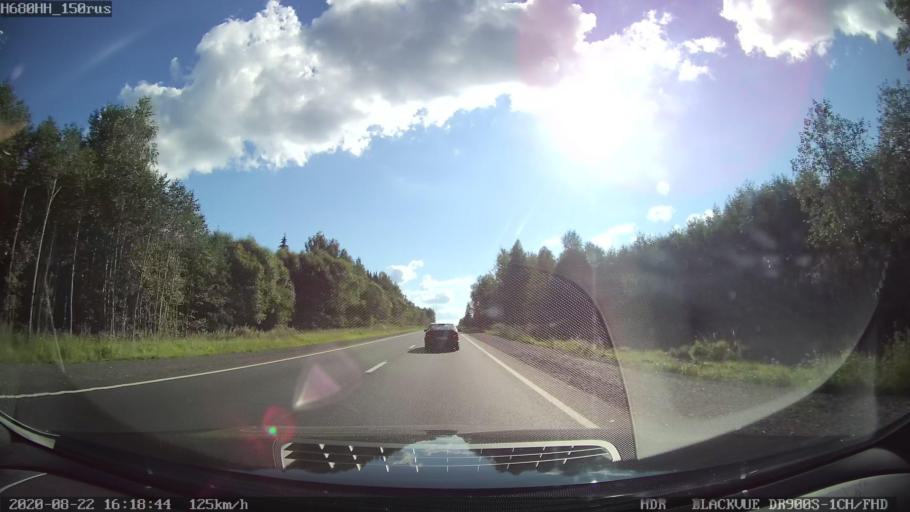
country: RU
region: Tverskaya
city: Rameshki
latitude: 57.4125
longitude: 36.1337
